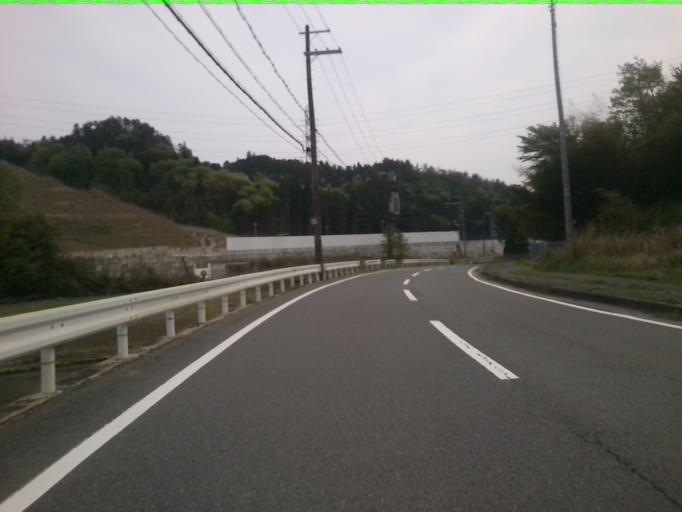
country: JP
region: Kyoto
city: Kameoka
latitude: 34.9636
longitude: 135.5585
